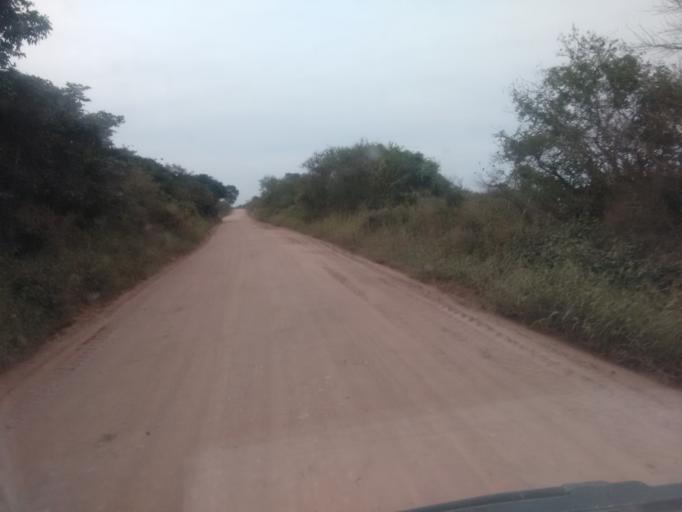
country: BR
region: Rio Grande do Sul
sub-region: Camaqua
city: Camaqua
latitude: -30.9761
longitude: -51.7948
